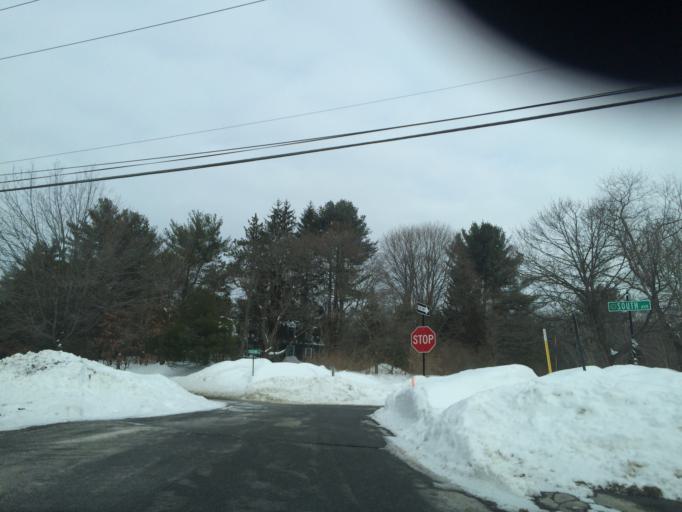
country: US
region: Massachusetts
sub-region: Middlesex County
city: Weston
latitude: 42.3382
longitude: -71.2901
